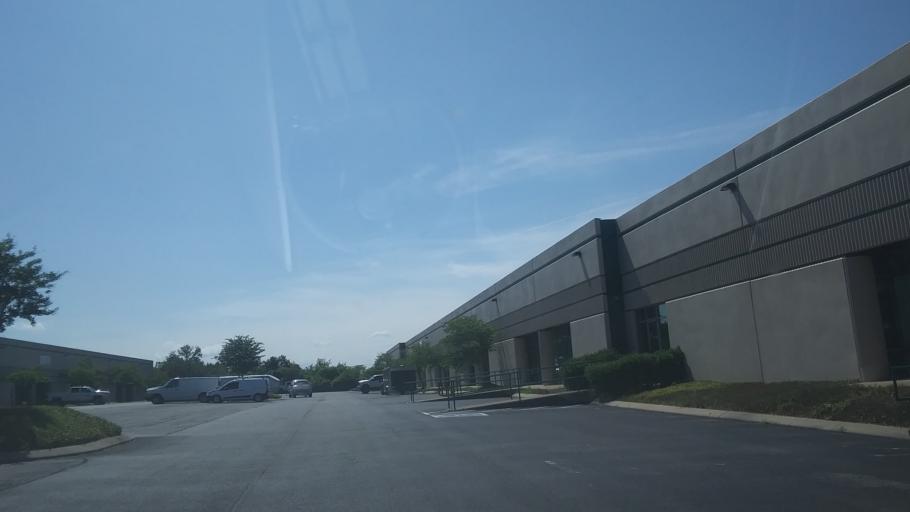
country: US
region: Tennessee
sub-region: Davidson County
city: Oak Hill
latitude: 36.0960
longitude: -86.6815
